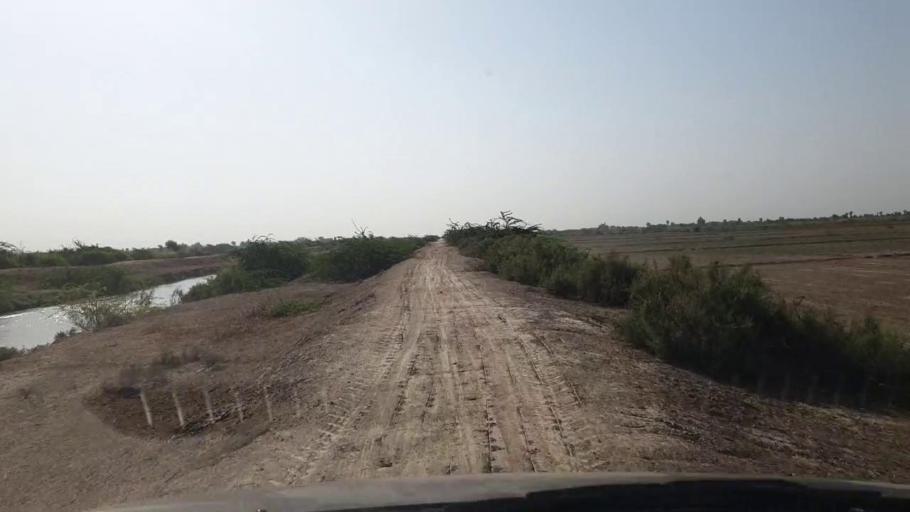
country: PK
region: Sindh
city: Kadhan
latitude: 24.5836
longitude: 69.0788
